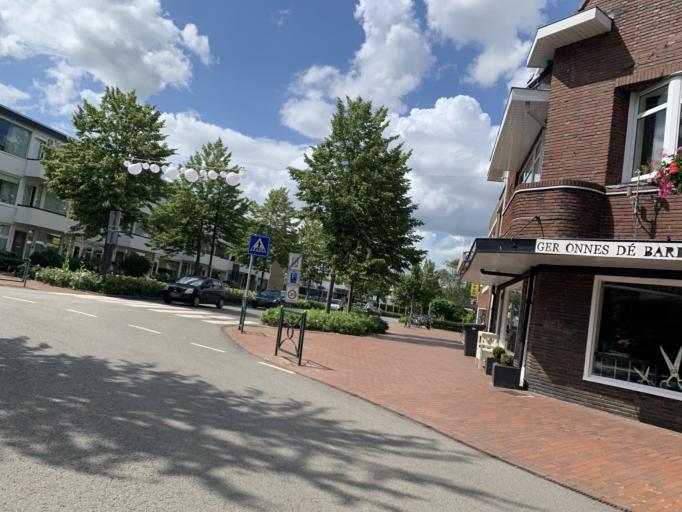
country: NL
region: Groningen
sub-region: Gemeente Haren
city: Haren
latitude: 53.1740
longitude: 6.6021
